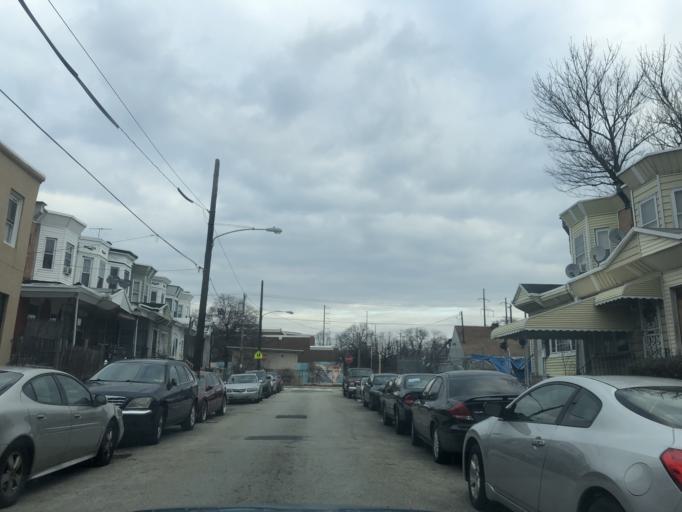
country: US
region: Pennsylvania
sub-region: Delaware County
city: Millbourne
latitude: 39.9764
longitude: -75.2290
